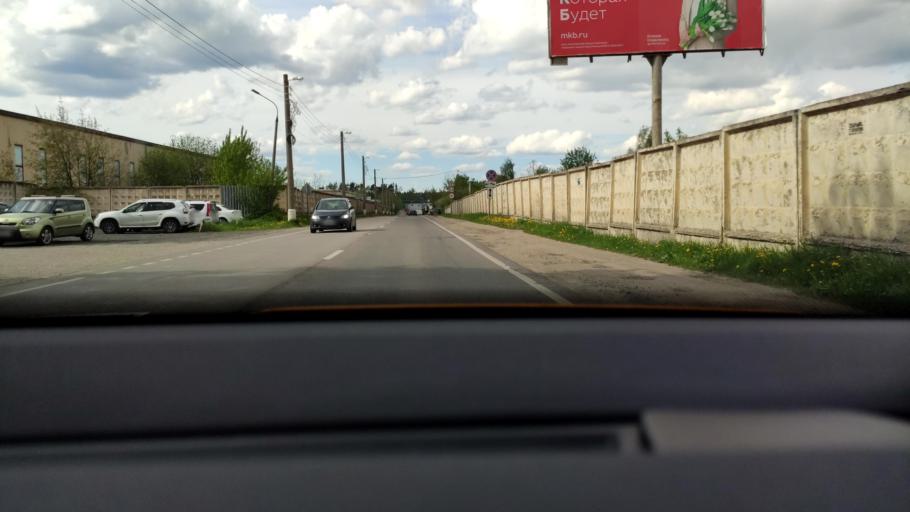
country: RU
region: Moskovskaya
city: Petrovo-Dal'neye
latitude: 55.7571
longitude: 37.1655
